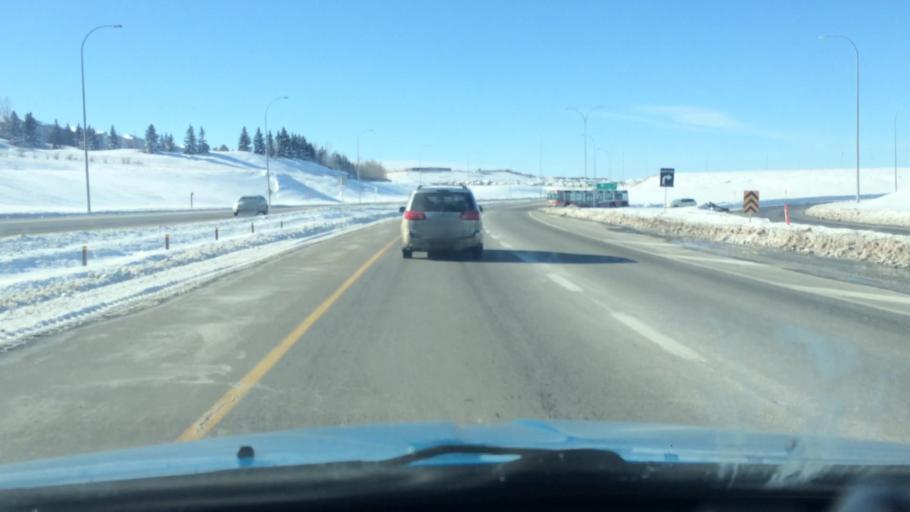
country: CA
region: Alberta
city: Calgary
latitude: 51.1471
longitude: -114.1343
